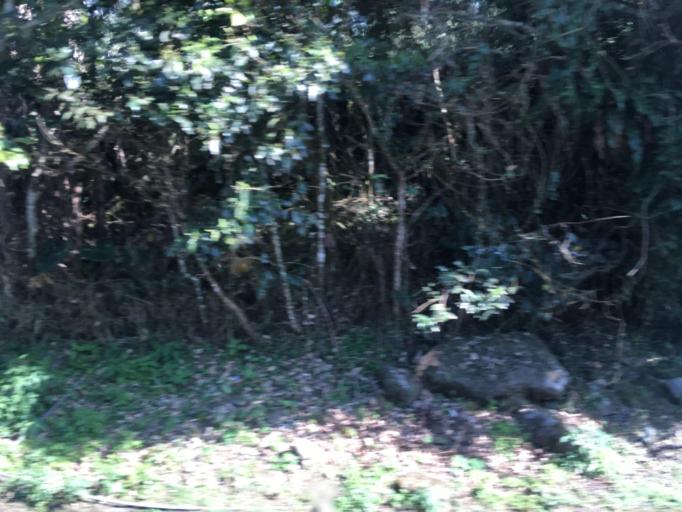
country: TW
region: Taiwan
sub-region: Chiayi
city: Jiayi Shi
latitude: 23.4262
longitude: 120.6431
